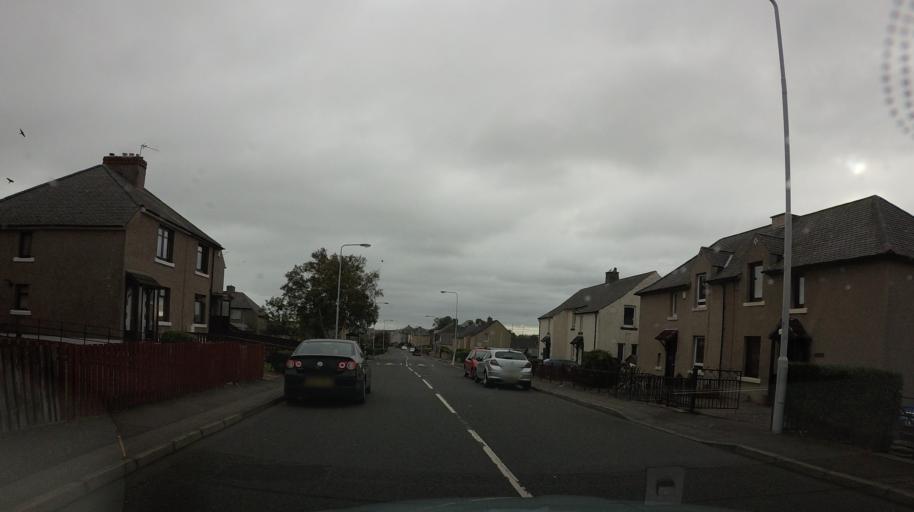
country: GB
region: Scotland
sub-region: Fife
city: Cowdenbeath
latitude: 56.1095
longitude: -3.3579
